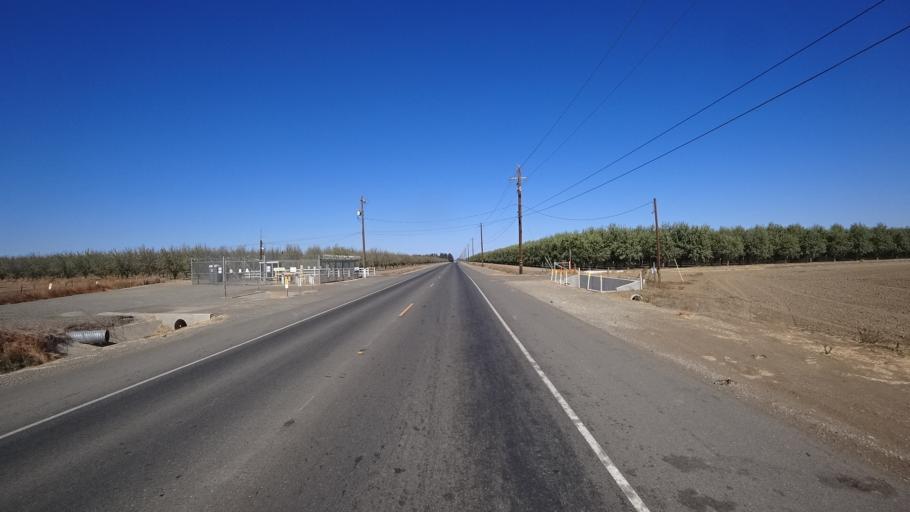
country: US
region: California
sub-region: Yolo County
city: Davis
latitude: 38.5975
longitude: -121.8034
